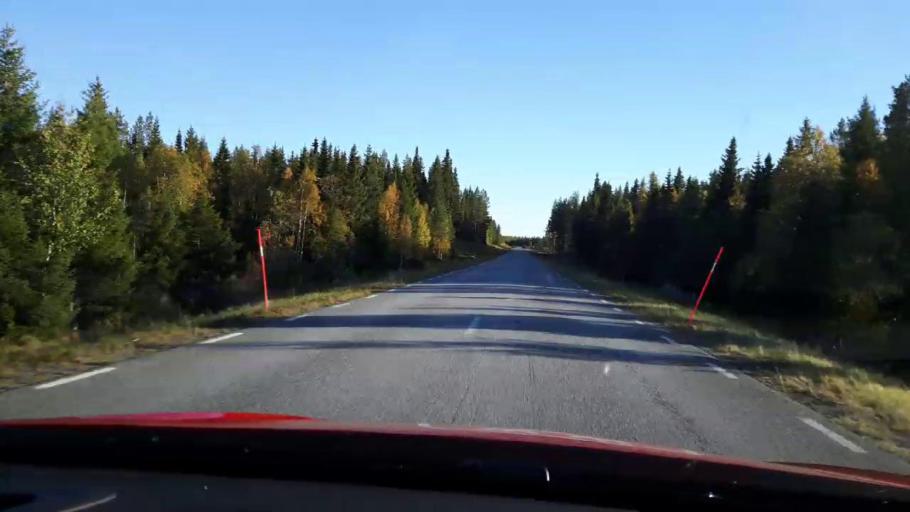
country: SE
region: Jaemtland
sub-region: OEstersunds Kommun
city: Lit
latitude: 63.7860
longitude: 14.7048
